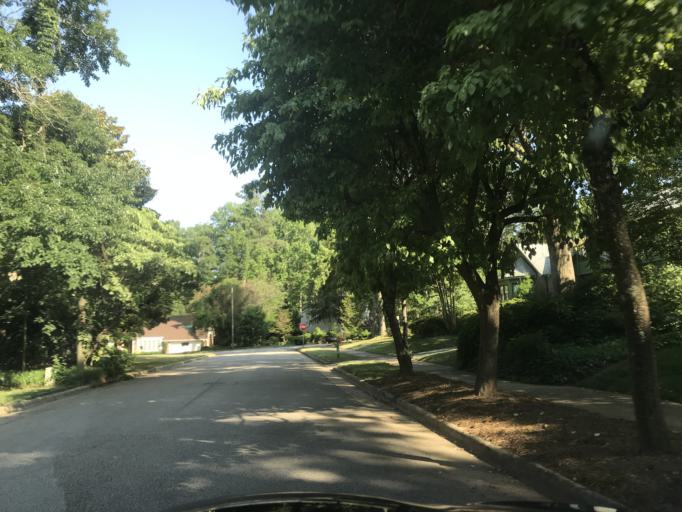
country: US
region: North Carolina
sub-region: Wake County
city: West Raleigh
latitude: 35.8728
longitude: -78.6090
